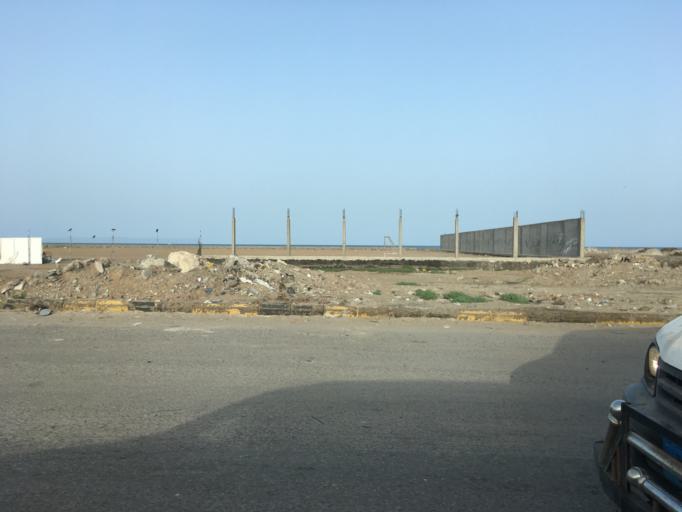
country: YE
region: Aden
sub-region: Khur Maksar
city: Khawr Maksar
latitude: 12.8350
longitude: 45.0477
